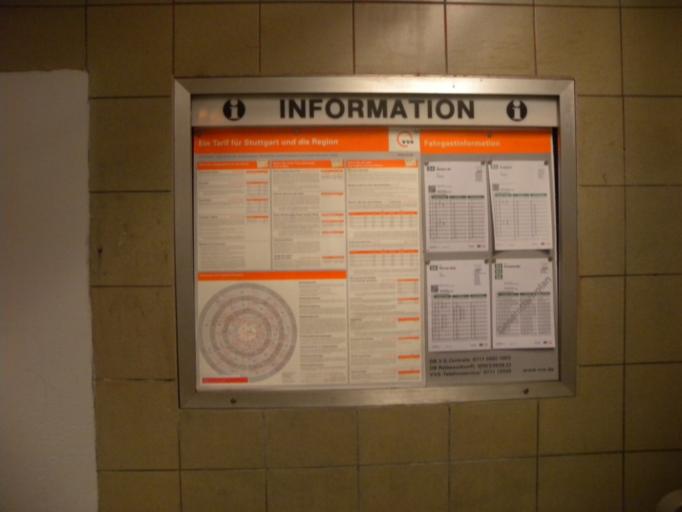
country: DE
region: Baden-Wuerttemberg
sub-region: Regierungsbezirk Stuttgart
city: Stuttgart
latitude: 48.8034
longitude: 9.1892
